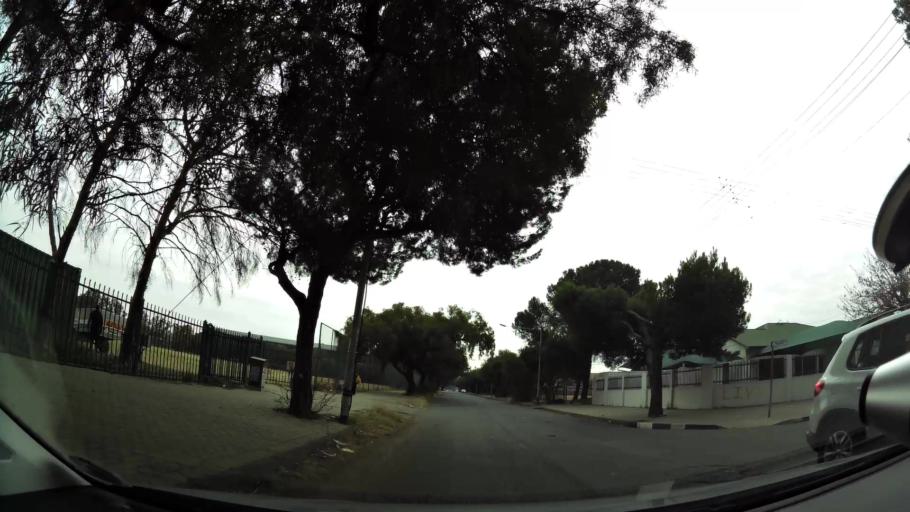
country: ZA
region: Orange Free State
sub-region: Mangaung Metropolitan Municipality
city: Bloemfontein
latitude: -29.1259
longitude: 26.2066
